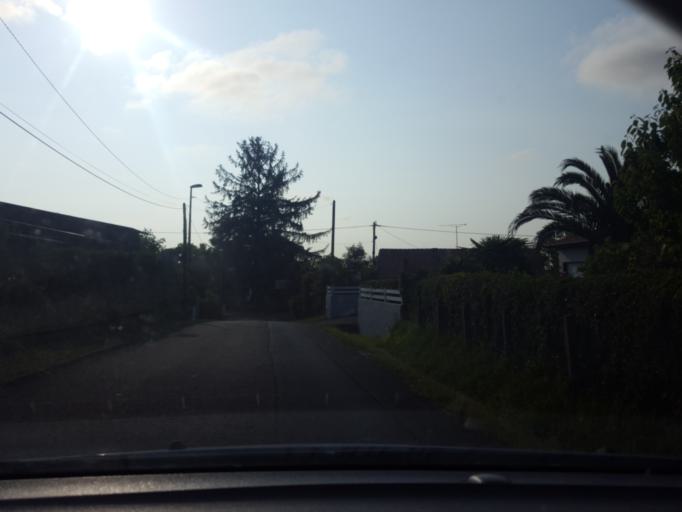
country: FR
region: Aquitaine
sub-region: Departement des Landes
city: Ondres
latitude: 43.5591
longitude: -1.4489
